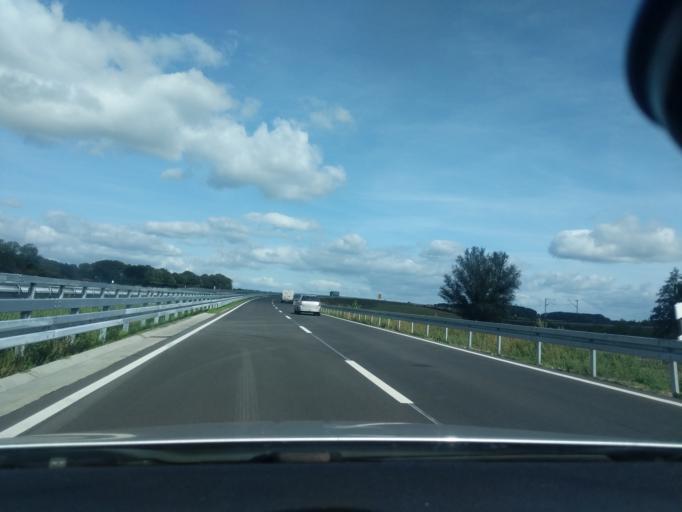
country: DE
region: Lower Saxony
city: Belm
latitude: 52.3187
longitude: 8.1386
